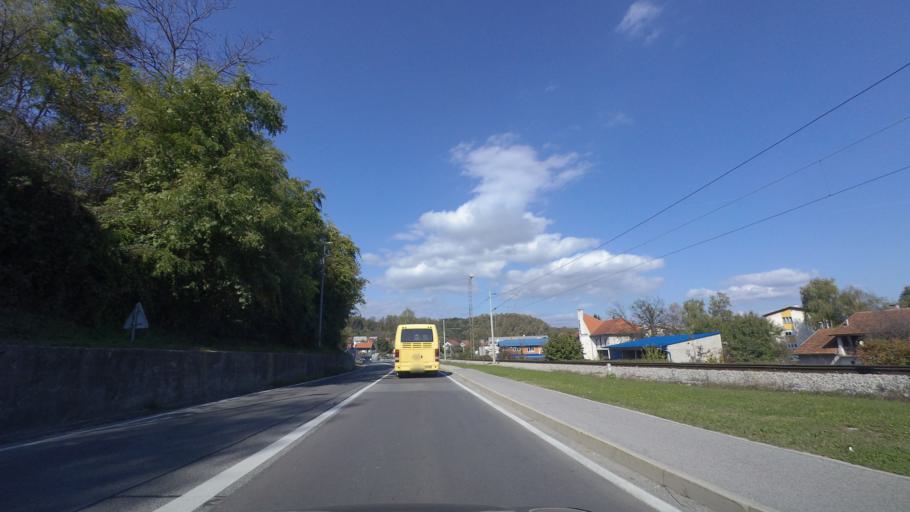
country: HR
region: Karlovacka
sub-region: Grad Karlovac
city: Karlovac
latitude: 45.4554
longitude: 15.4916
